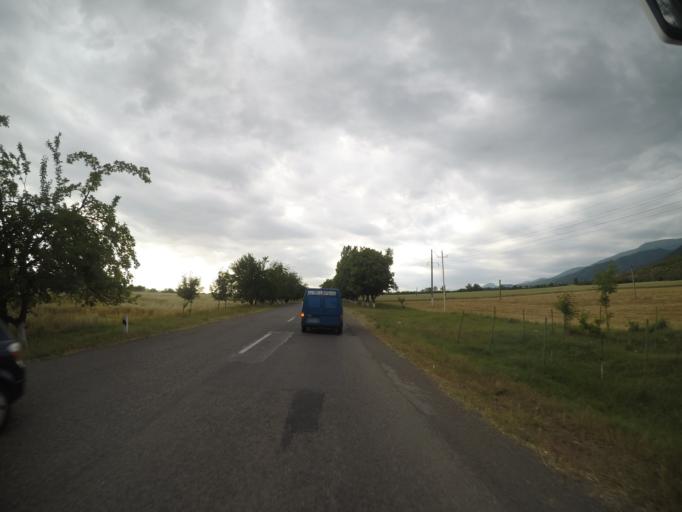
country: AZ
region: Ismayilli
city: Ismayilli
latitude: 40.7726
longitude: 48.2033
